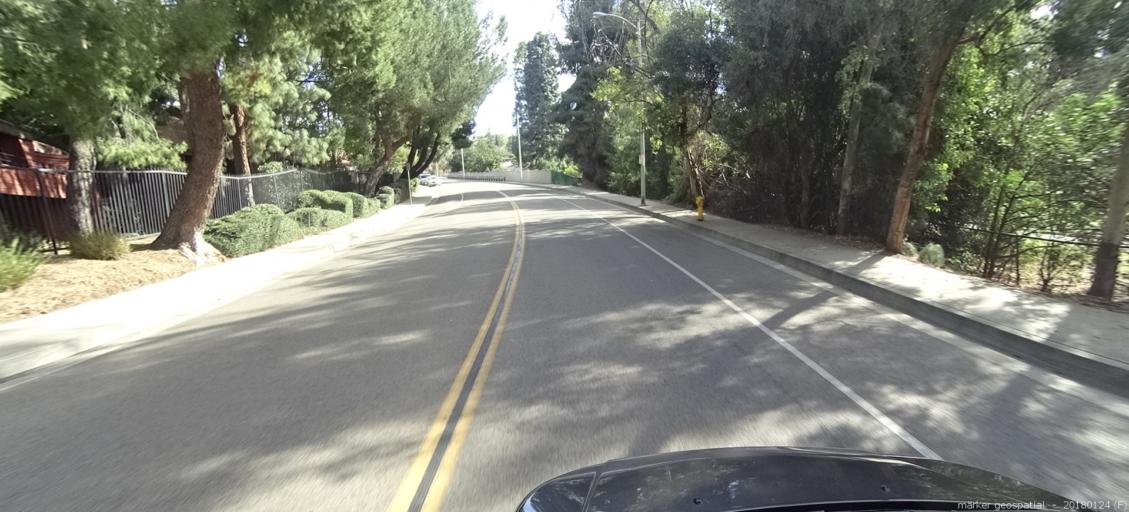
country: US
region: California
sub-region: Los Angeles County
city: Diamond Bar
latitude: 34.0182
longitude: -117.8134
